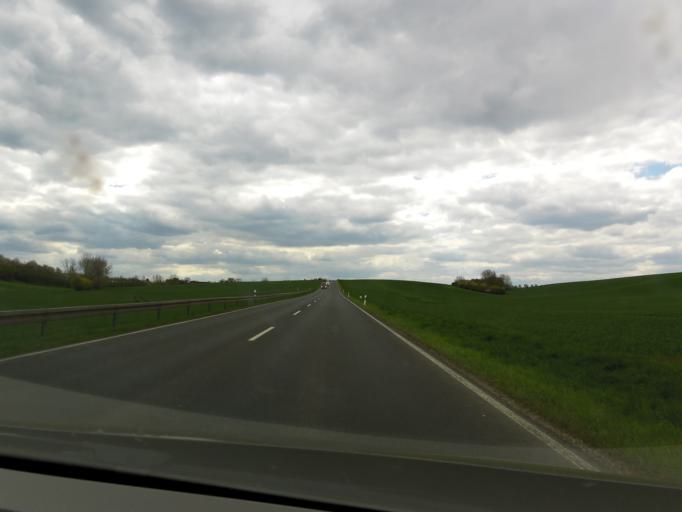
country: DE
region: Thuringia
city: Rannstedt
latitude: 51.0959
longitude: 11.5444
